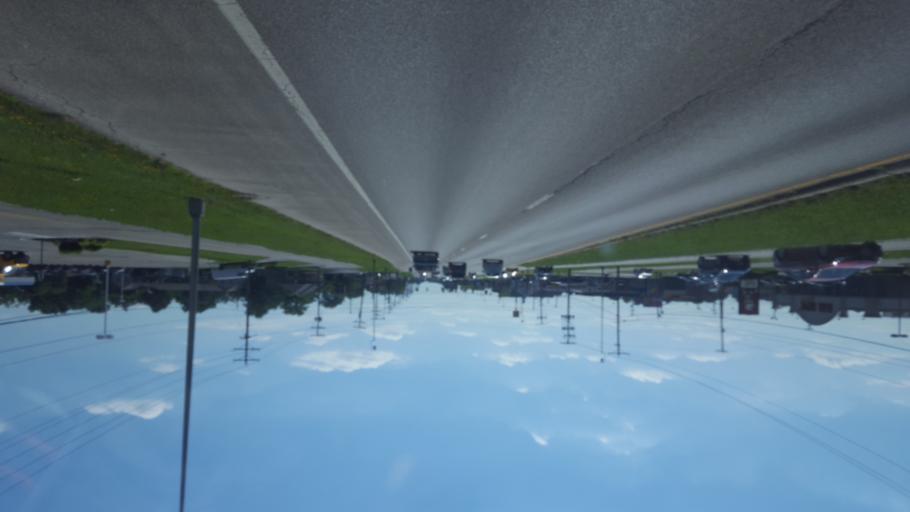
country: US
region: Ohio
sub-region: Franklin County
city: Minerva Park
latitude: 40.0871
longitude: -82.9727
